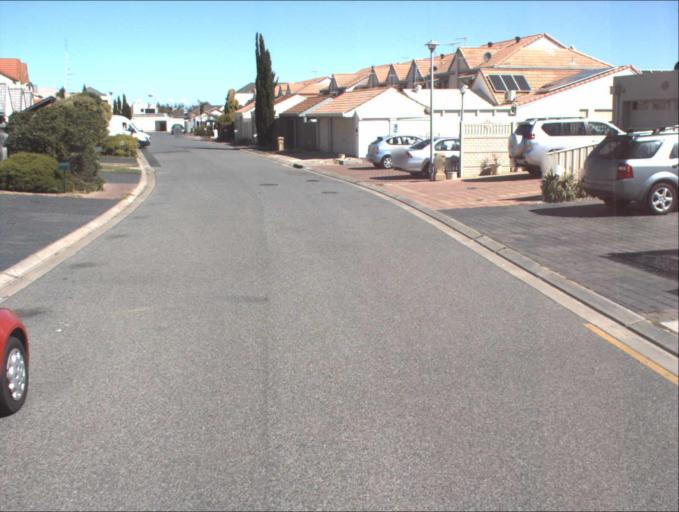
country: AU
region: South Australia
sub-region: Port Adelaide Enfield
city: Birkenhead
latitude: -34.7927
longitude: 138.4871
